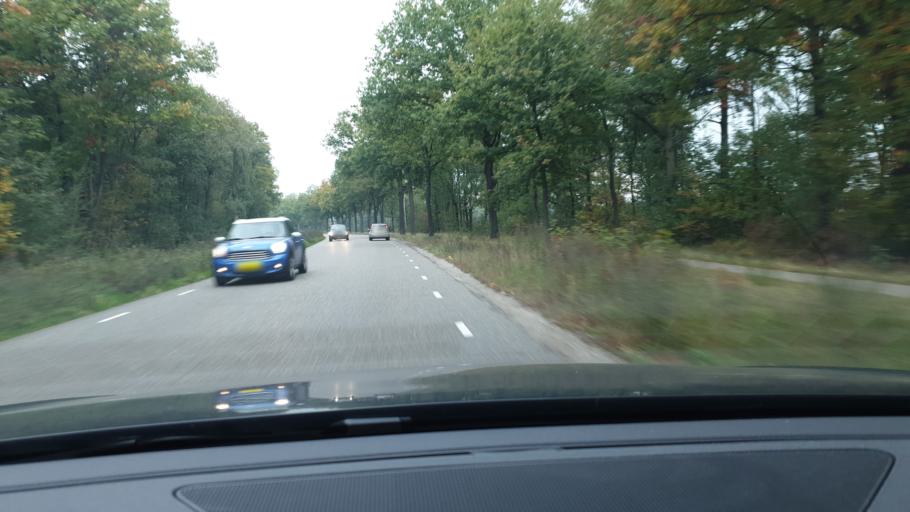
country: NL
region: North Brabant
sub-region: Gemeente Eersel
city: Eersel
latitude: 51.3676
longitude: 5.2874
